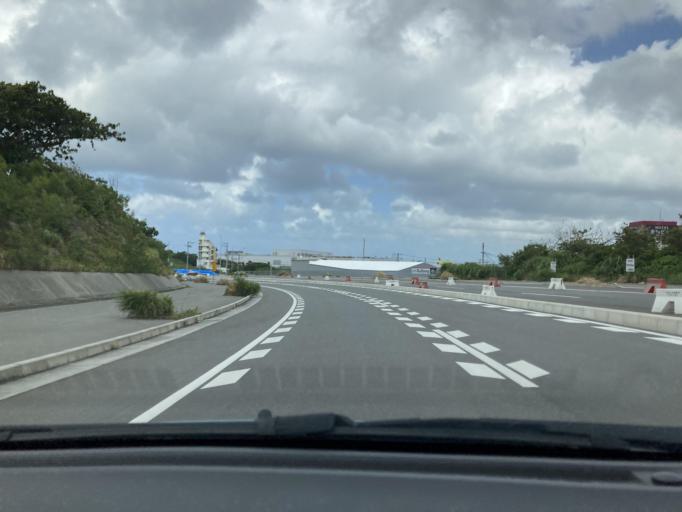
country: JP
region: Okinawa
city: Ginowan
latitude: 26.2676
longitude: 127.7098
